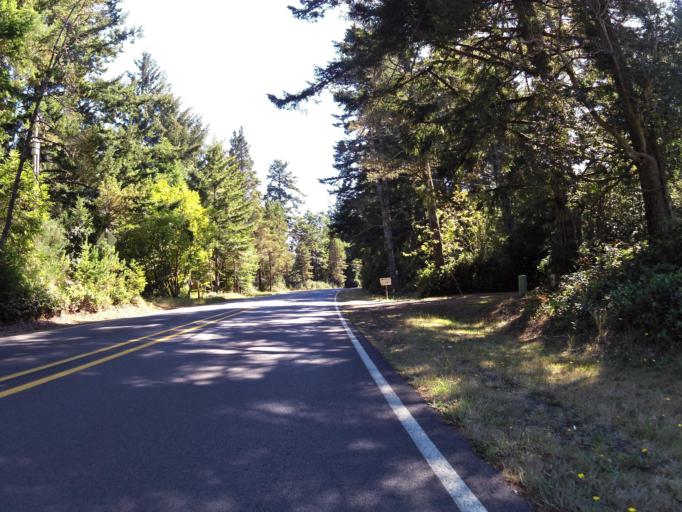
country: US
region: Oregon
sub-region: Coos County
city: Bandon
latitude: 43.2120
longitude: -124.3695
